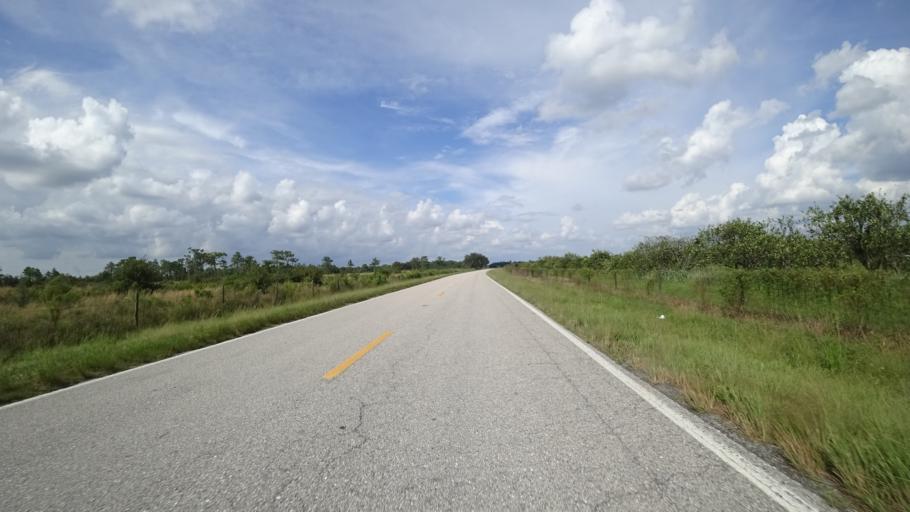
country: US
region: Florida
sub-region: Hillsborough County
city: Wimauma
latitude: 27.5430
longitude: -82.1040
